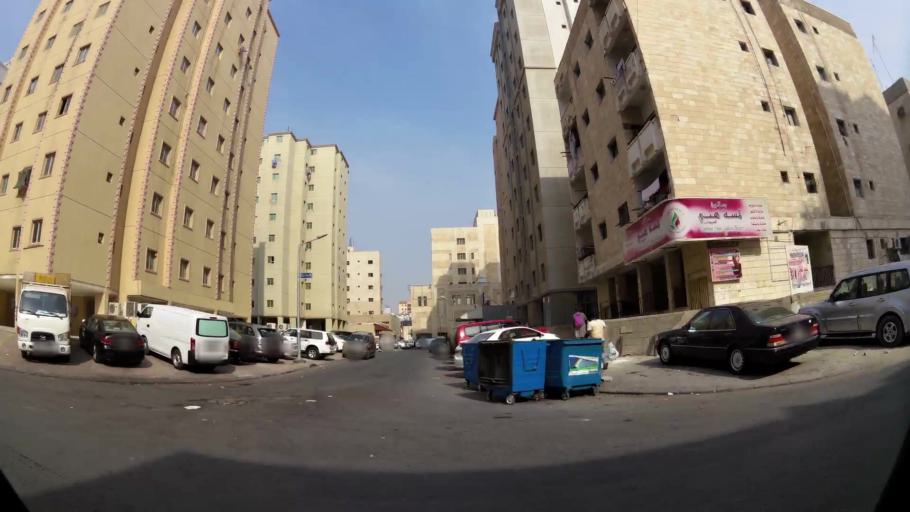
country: KW
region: Al Farwaniyah
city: Al Farwaniyah
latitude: 29.2784
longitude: 47.9585
